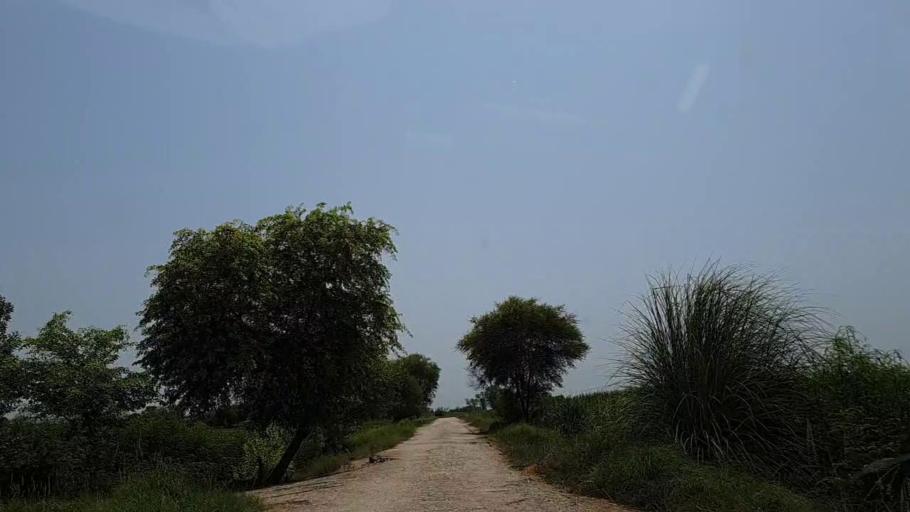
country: PK
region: Sindh
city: Ghotki
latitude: 27.9777
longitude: 69.4018
